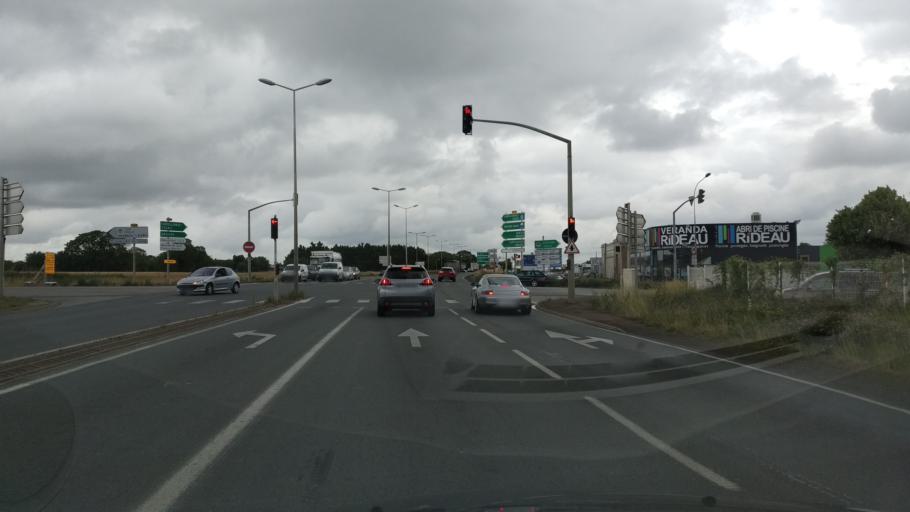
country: FR
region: Poitou-Charentes
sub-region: Departement de la Vienne
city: Poitiers
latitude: 46.5992
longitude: 0.3212
